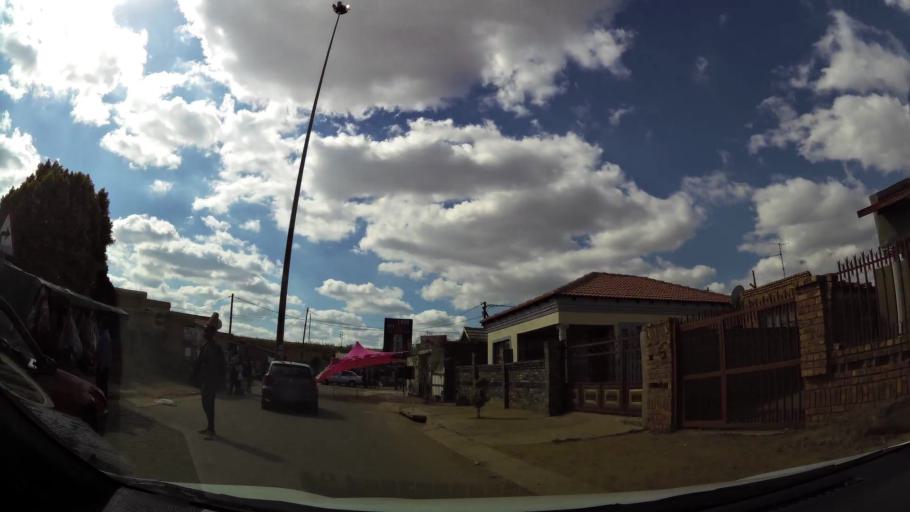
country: ZA
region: Gauteng
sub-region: City of Tshwane Metropolitan Municipality
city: Cullinan
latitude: -25.7053
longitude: 28.4024
